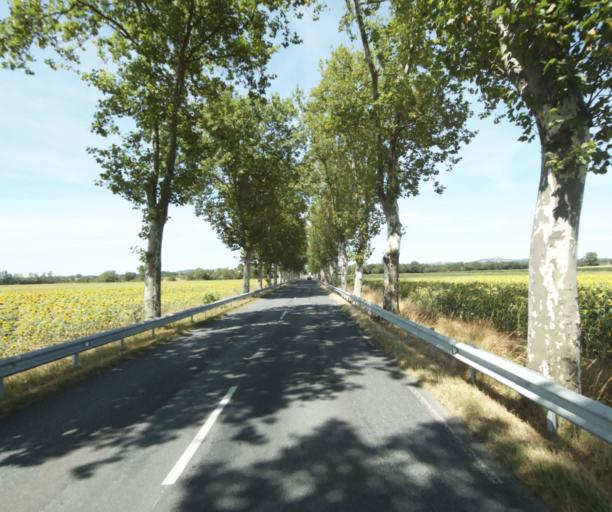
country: FR
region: Midi-Pyrenees
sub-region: Departement de la Haute-Garonne
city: Revel
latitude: 43.5081
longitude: 2.0110
